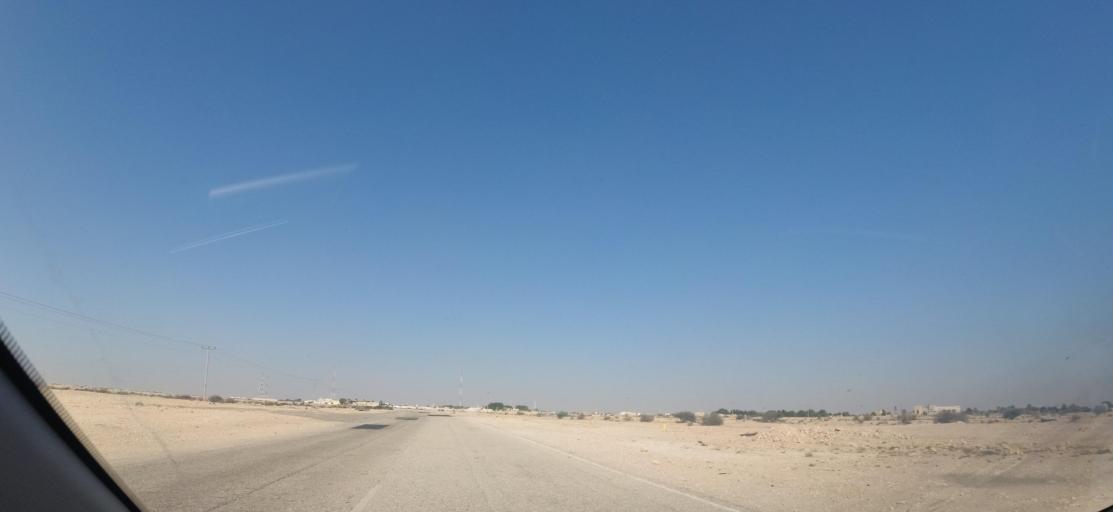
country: QA
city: Al Jumayliyah
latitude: 25.6088
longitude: 51.0774
